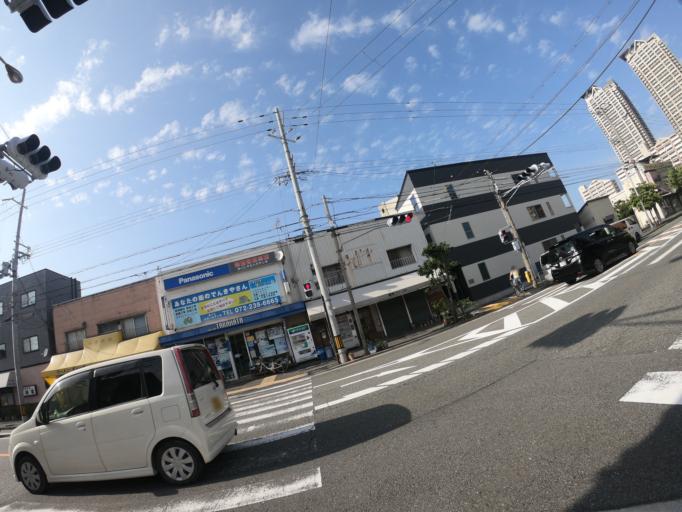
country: JP
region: Osaka
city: Sakai
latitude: 34.5772
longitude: 135.4924
